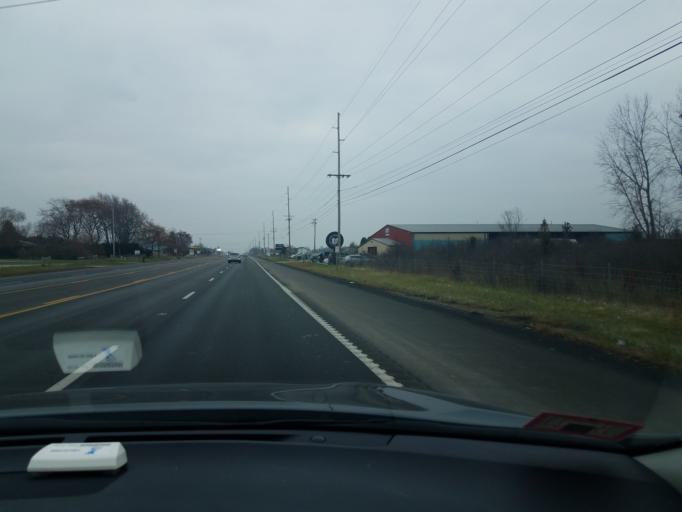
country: US
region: Ohio
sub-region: Erie County
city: Sandusky
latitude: 41.3937
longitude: -82.6507
